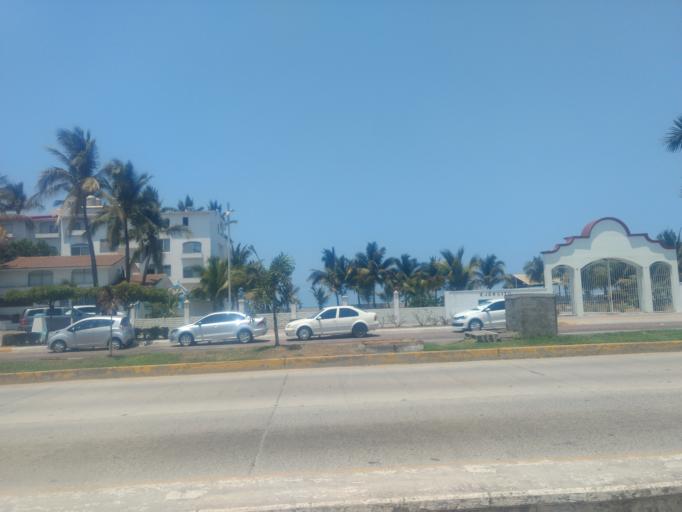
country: MX
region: Colima
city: Tapeixtles
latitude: 19.0873
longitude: -104.3108
